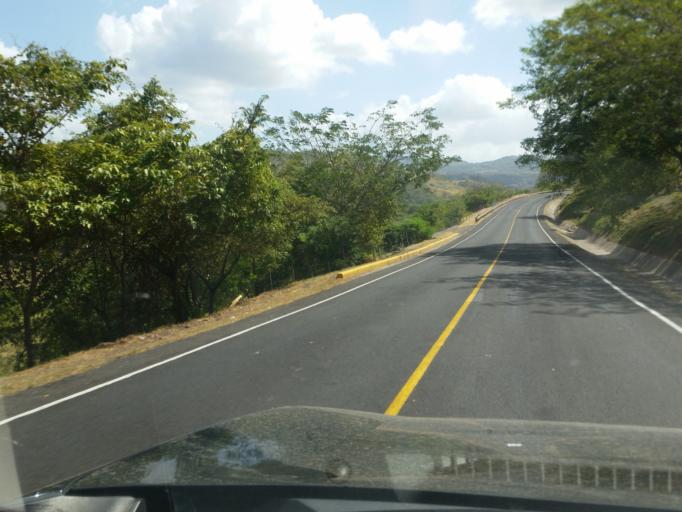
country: NI
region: Boaco
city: San Lorenzo
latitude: 12.2632
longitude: -85.6464
